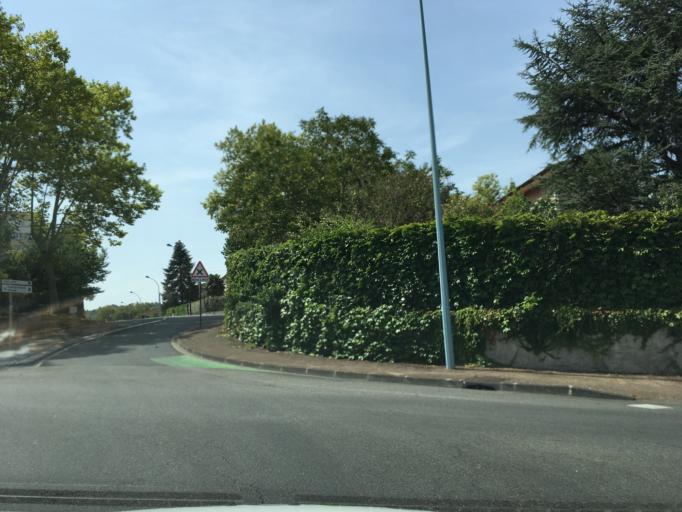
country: FR
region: Midi-Pyrenees
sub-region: Departement du Tarn
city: Castres
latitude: 43.6162
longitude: 2.2364
